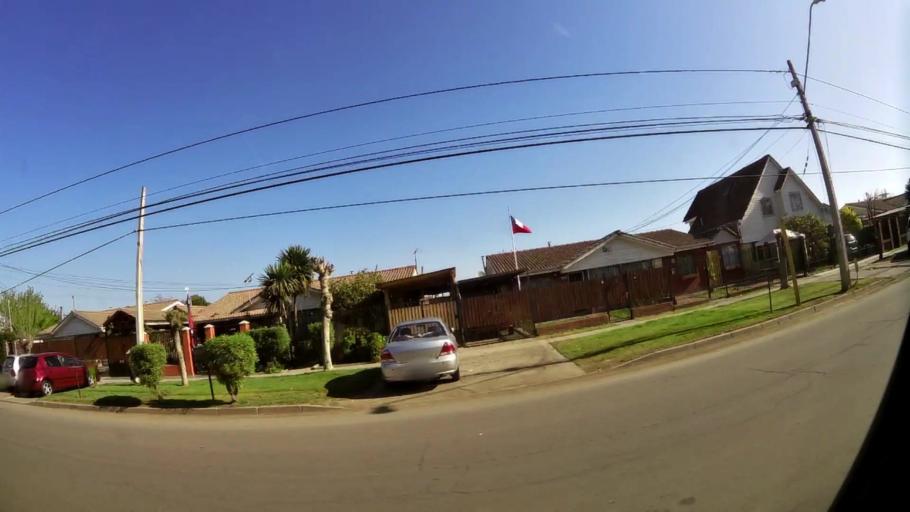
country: CL
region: Santiago Metropolitan
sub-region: Provincia de Santiago
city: Lo Prado
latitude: -33.4883
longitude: -70.7778
